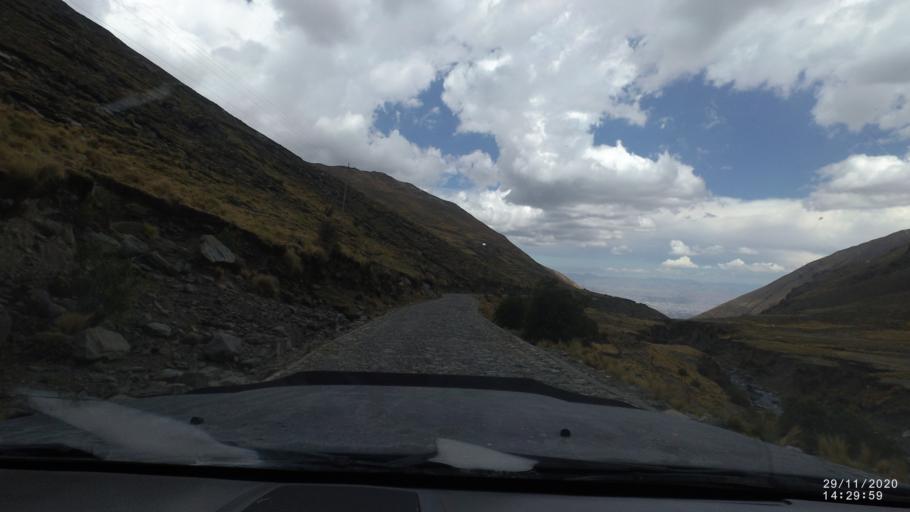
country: BO
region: Cochabamba
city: Sipe Sipe
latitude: -17.2628
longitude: -66.3520
